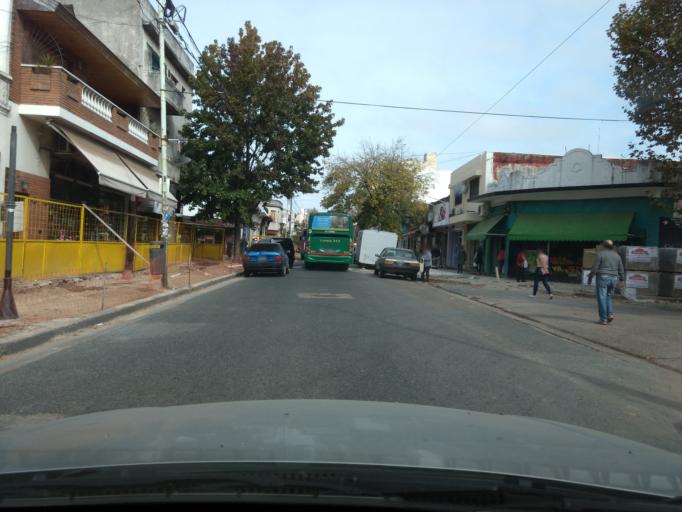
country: AR
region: Buenos Aires F.D.
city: Villa Santa Rita
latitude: -34.6231
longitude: -58.5103
